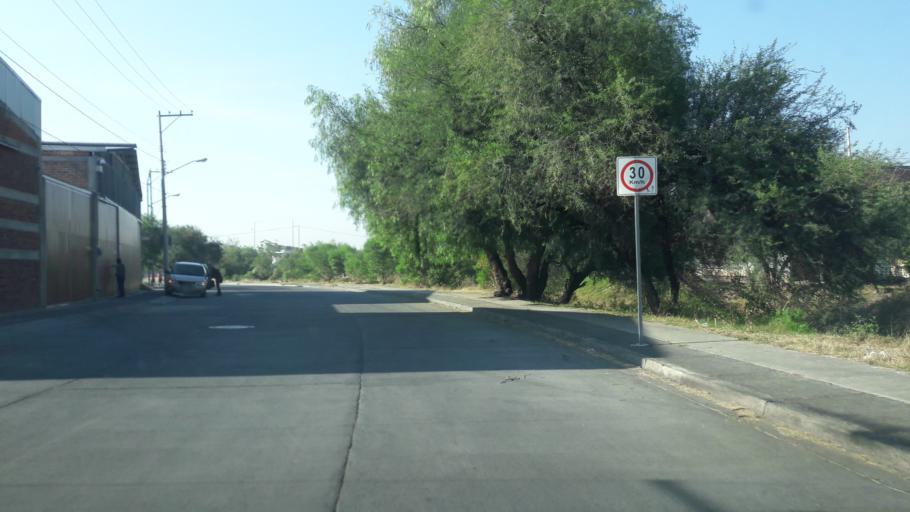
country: MX
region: Guanajuato
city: Leon
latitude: 21.1751
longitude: -101.6707
